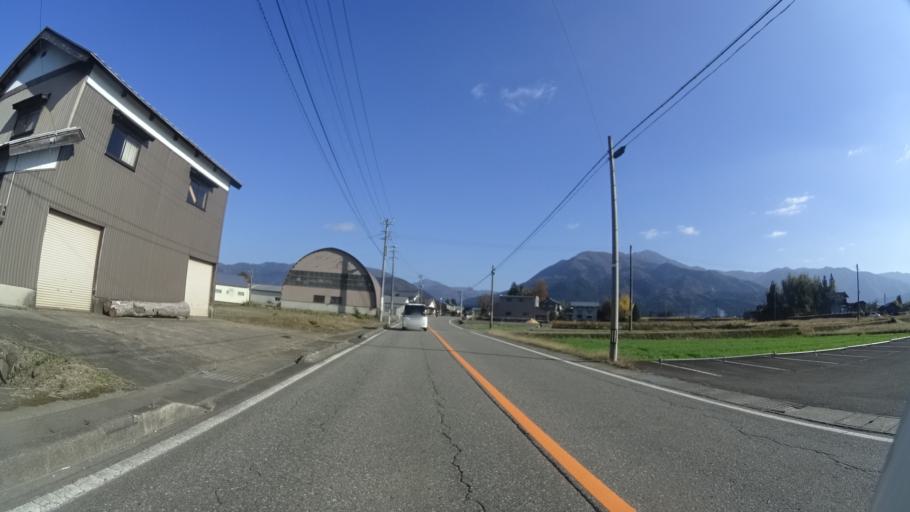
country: JP
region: Fukui
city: Ono
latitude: 35.9783
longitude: 136.5384
